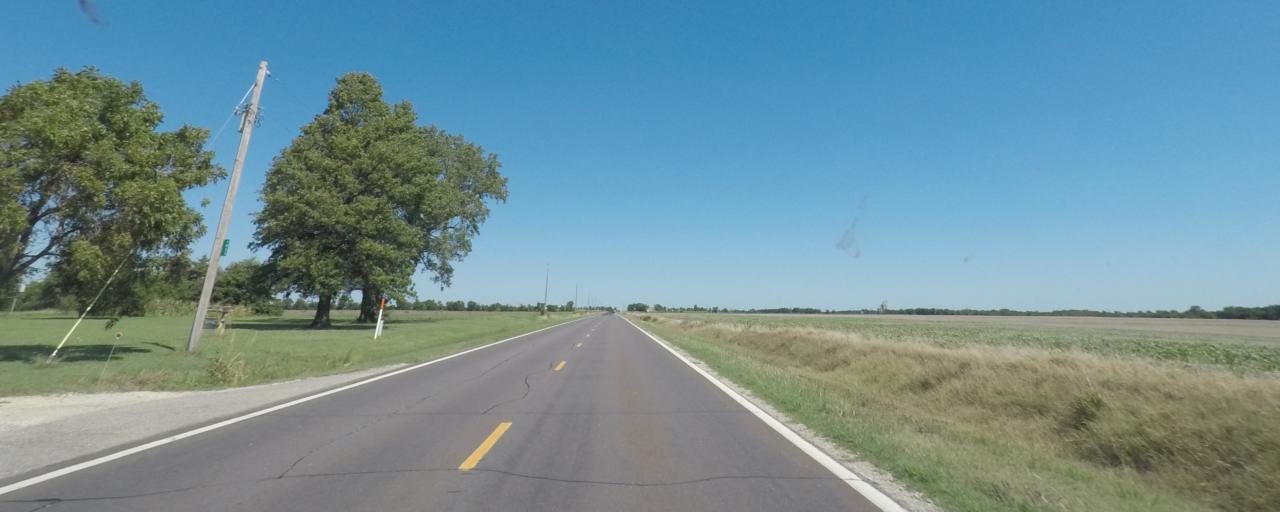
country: US
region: Kansas
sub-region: Sumner County
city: Wellington
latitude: 37.1385
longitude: -97.4021
